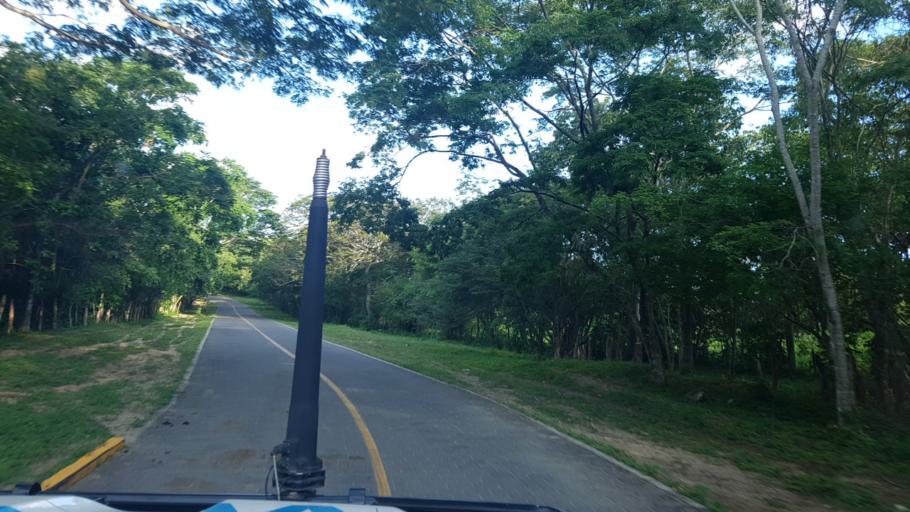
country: NI
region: Nueva Segovia
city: Ocotal
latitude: 13.6420
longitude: -86.5885
